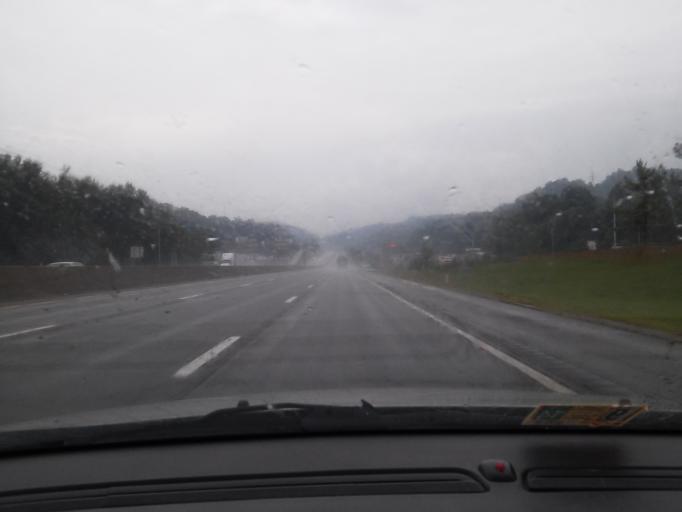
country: US
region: West Virginia
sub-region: Kanawha County
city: Cross Lanes
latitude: 38.4123
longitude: -81.7958
